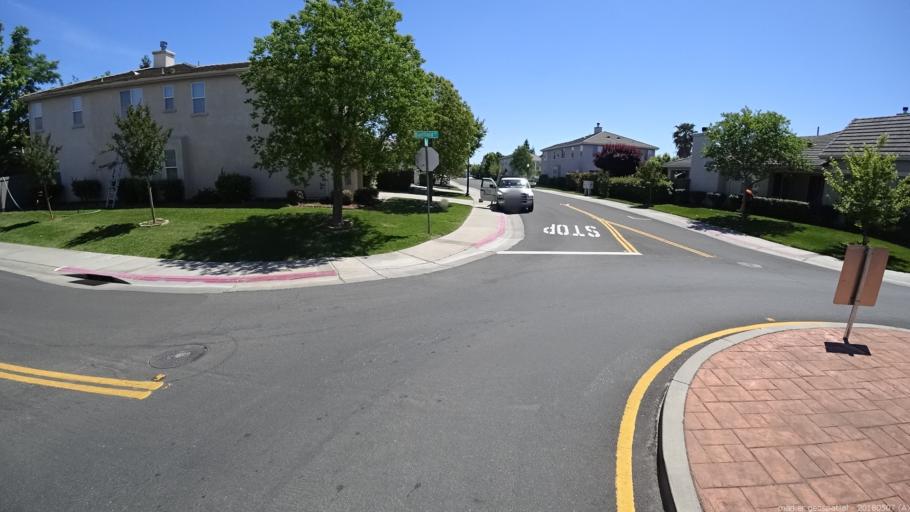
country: US
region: California
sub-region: Sacramento County
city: Elverta
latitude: 38.6735
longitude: -121.5105
